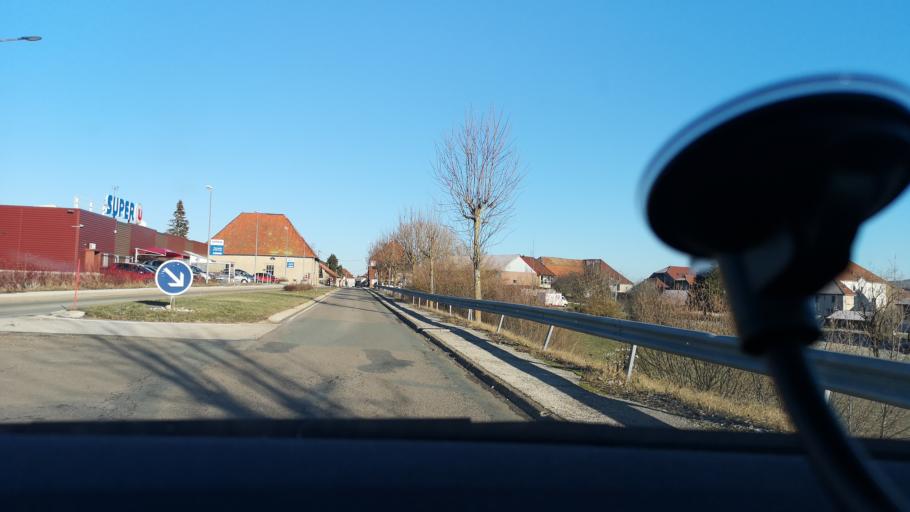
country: FR
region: Franche-Comte
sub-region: Departement du Doubs
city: Frasne
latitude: 46.8523
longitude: 6.1520
